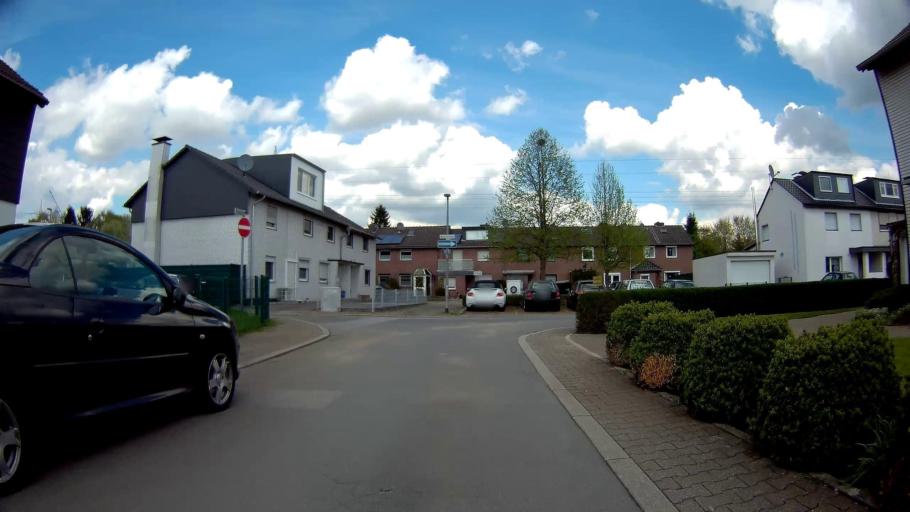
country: DE
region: North Rhine-Westphalia
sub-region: Regierungsbezirk Munster
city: Gladbeck
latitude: 51.5545
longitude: 7.0221
